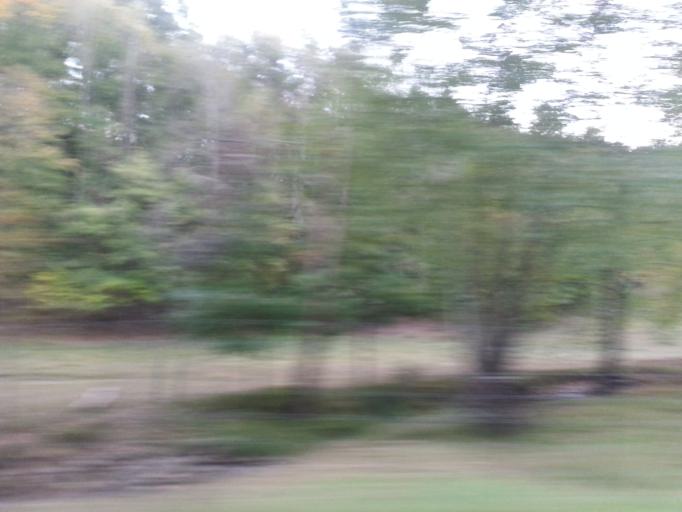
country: US
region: Tennessee
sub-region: Blount County
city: Wildwood
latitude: 35.7690
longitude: -83.8044
